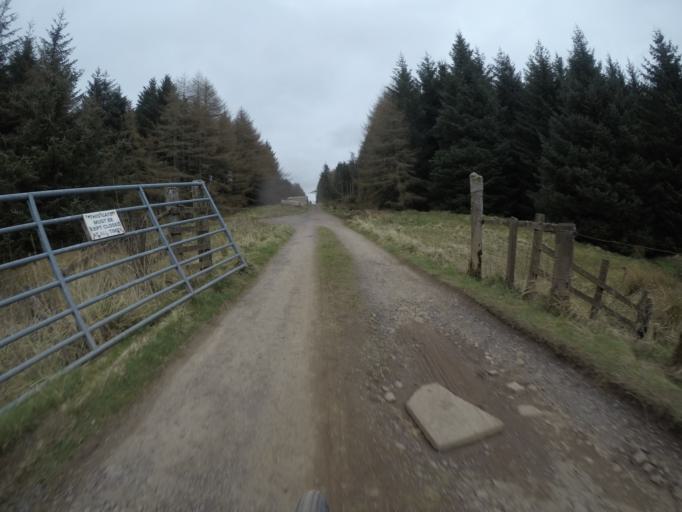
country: GB
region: Scotland
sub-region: East Ayrshire
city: Newmilns
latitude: 55.6596
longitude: -4.3399
